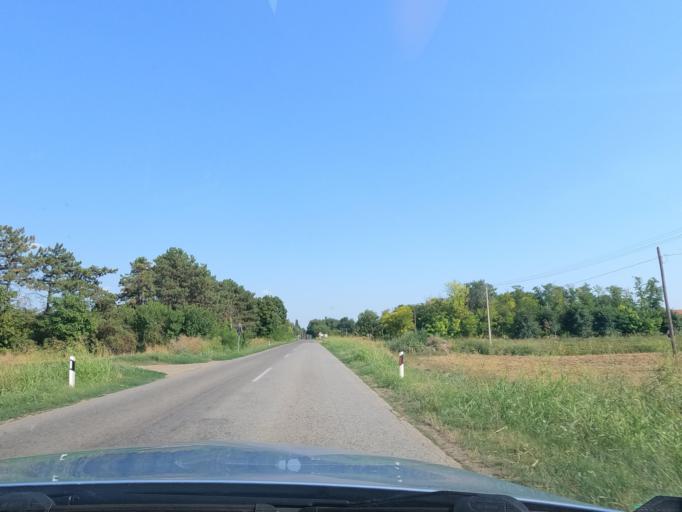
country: RS
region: Autonomna Pokrajina Vojvodina
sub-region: Juznobacki Okrug
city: Becej
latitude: 45.6321
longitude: 20.0143
